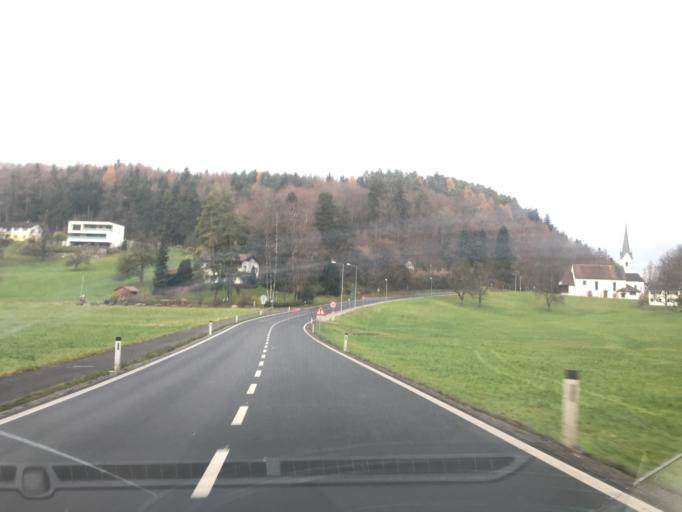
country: AT
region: Vorarlberg
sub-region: Politischer Bezirk Feldkirch
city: Klaus
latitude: 47.3228
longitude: 9.6438
